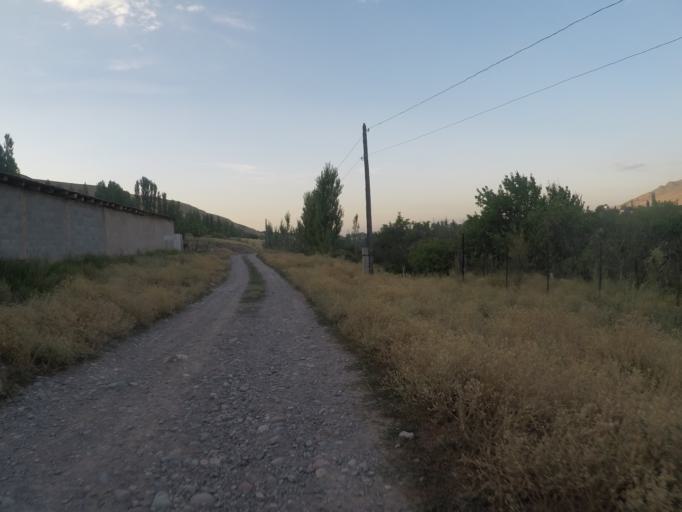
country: KG
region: Chuy
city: Bishkek
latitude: 42.7723
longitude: 74.6399
